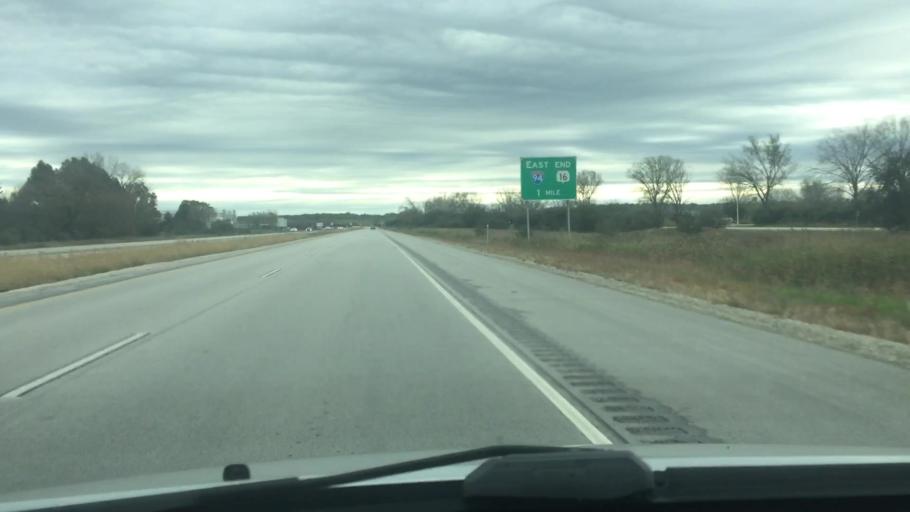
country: US
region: Wisconsin
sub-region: Waukesha County
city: Pewaukee
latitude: 43.0588
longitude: -88.2513
